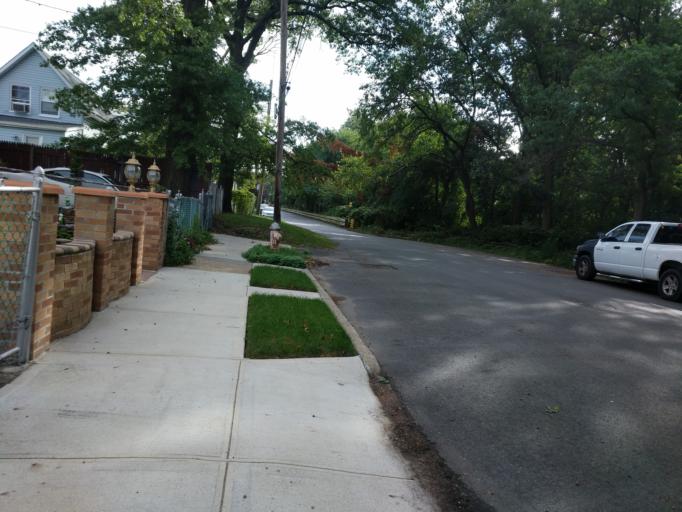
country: US
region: New York
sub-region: Queens County
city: Jamaica
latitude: 40.6796
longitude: -73.7700
